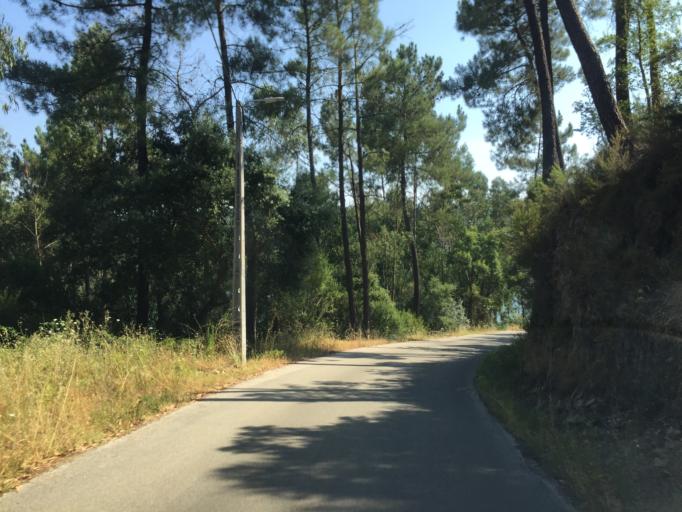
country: PT
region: Santarem
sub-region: Ferreira do Zezere
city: Ferreira do Zezere
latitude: 39.6087
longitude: -8.2819
